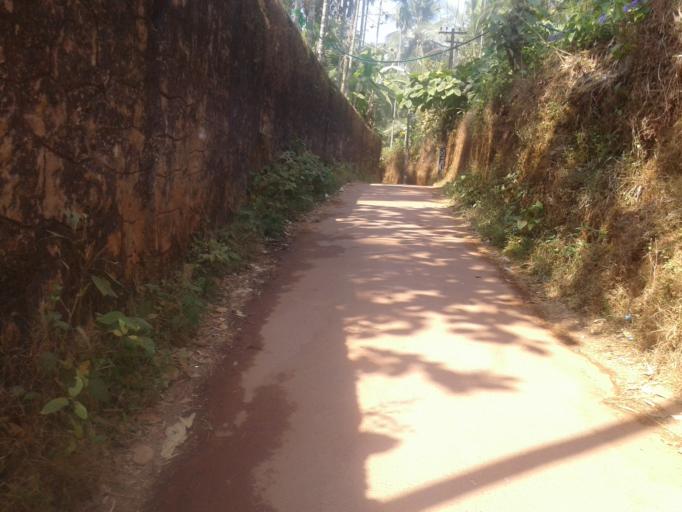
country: IN
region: Kerala
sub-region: Kozhikode
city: Nadapuram
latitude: 11.6868
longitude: 75.6760
